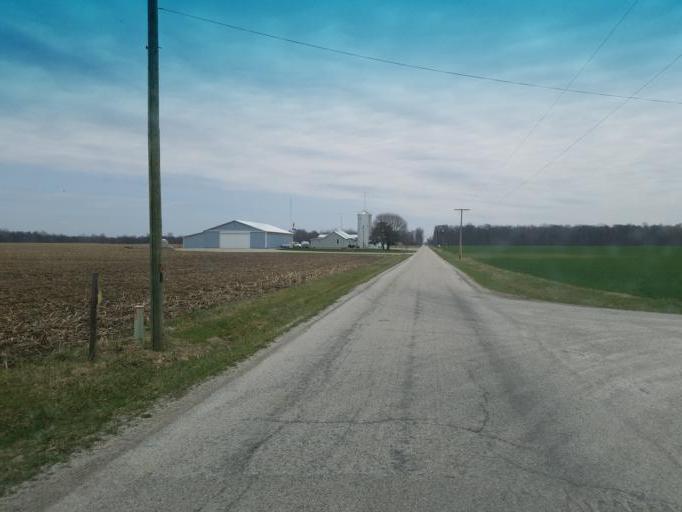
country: US
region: Ohio
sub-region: Crawford County
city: Bucyrus
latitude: 40.8920
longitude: -82.9787
